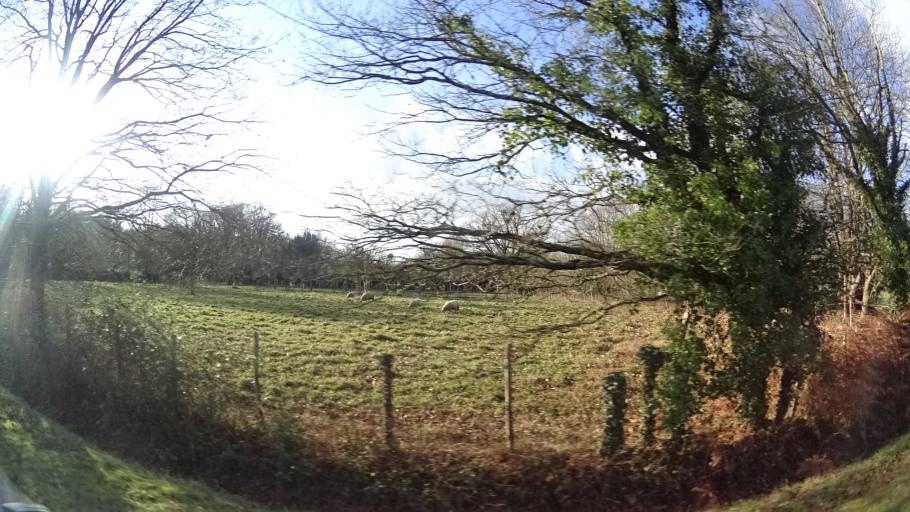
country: FR
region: Pays de la Loire
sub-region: Departement de la Loire-Atlantique
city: Plesse
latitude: 47.5639
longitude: -1.8688
